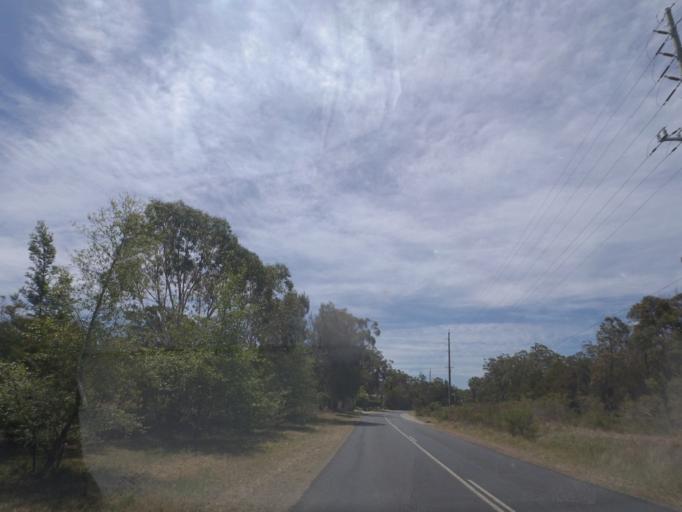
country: AU
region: New South Wales
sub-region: Wingecarribee
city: Colo Vale
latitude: -34.3860
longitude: 150.5307
